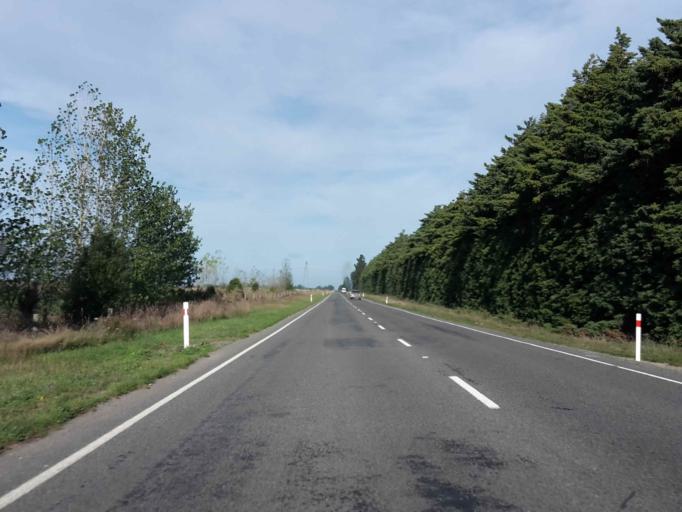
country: NZ
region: Canterbury
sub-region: Timaru District
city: Pleasant Point
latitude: -44.0493
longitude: 171.3285
